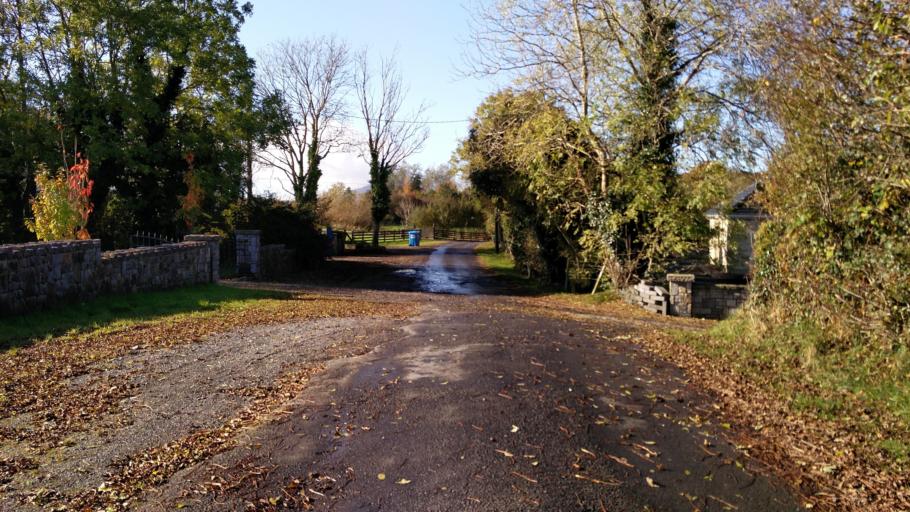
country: IE
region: Connaught
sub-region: Maigh Eo
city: Westport
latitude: 53.7798
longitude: -9.4428
